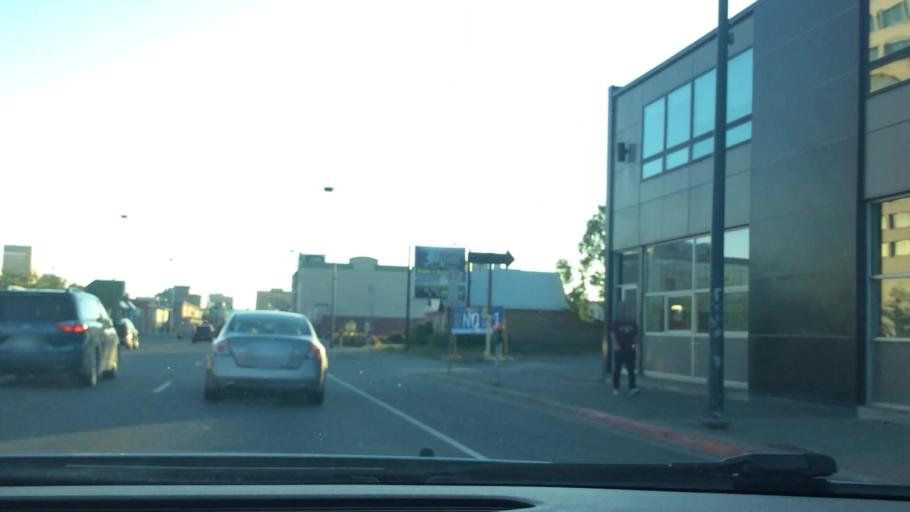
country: US
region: Alaska
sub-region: Anchorage Municipality
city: Anchorage
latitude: 61.2176
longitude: -149.8752
